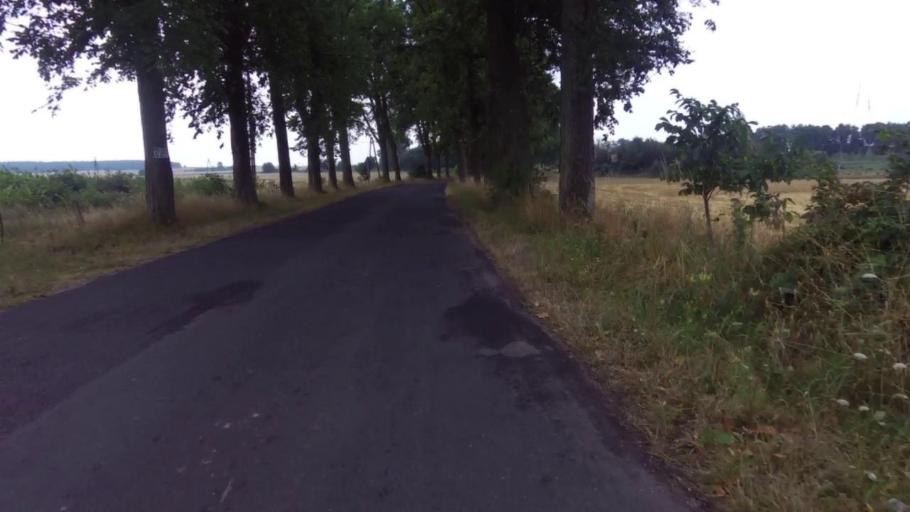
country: PL
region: West Pomeranian Voivodeship
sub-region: Powiat choszczenski
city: Choszczno
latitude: 53.2087
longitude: 15.3927
